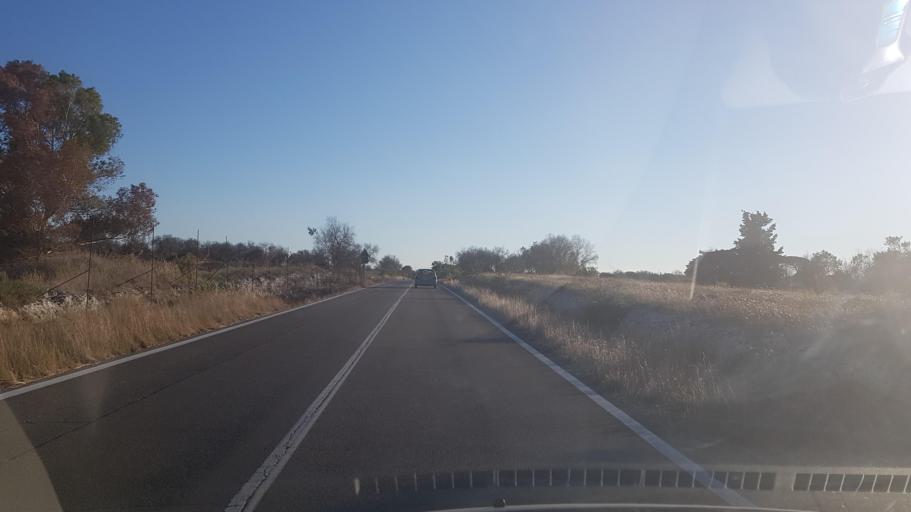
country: IT
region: Apulia
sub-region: Provincia di Lecce
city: Vernole
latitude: 40.3264
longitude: 18.3316
